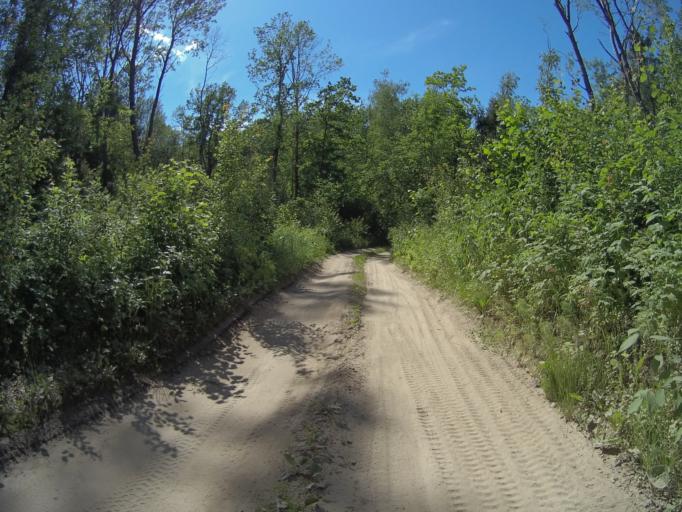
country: RU
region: Vladimir
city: Raduzhnyy
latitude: 55.9877
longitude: 40.3751
